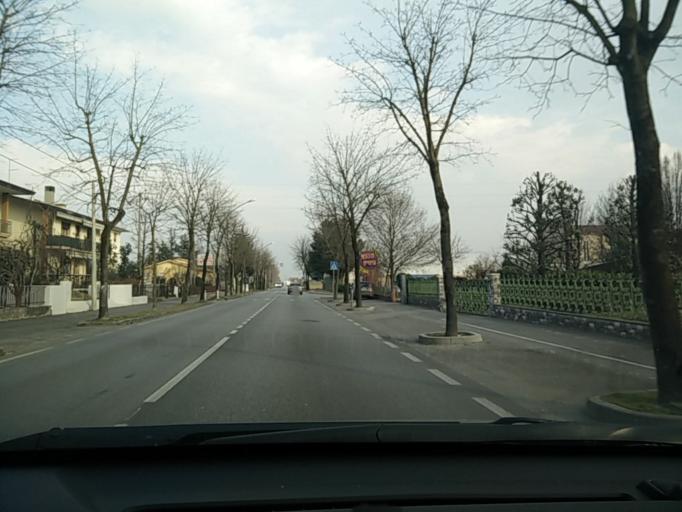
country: IT
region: Veneto
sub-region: Provincia di Treviso
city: San Vendemiano
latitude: 45.8749
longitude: 12.3478
